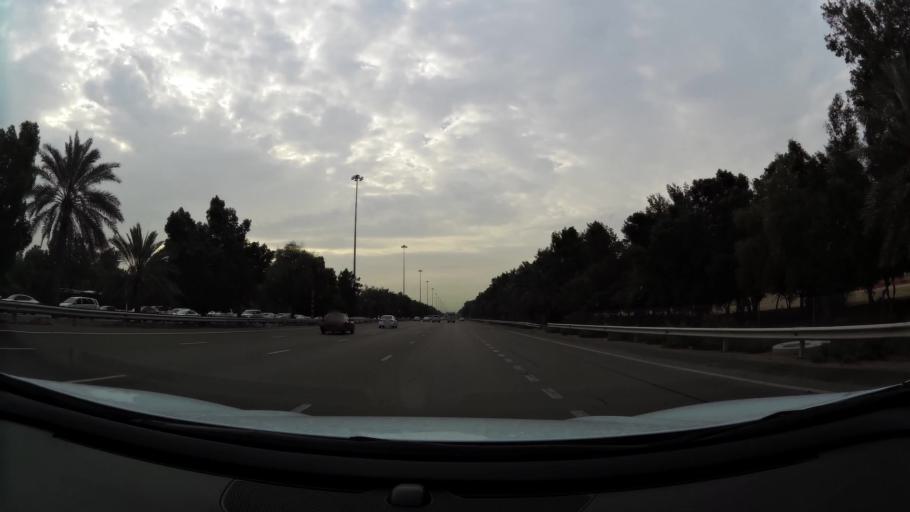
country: AE
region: Abu Dhabi
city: Abu Dhabi
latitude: 24.3441
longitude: 54.5741
